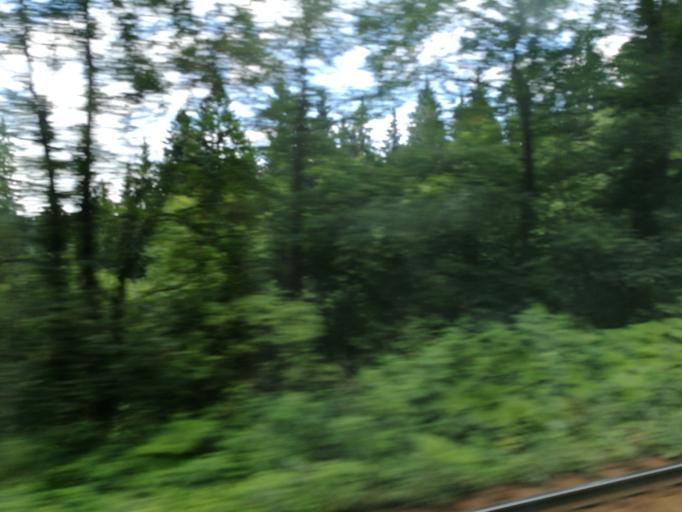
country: RO
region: Brasov
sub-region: Oras Predeal
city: Predeal
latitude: 45.5217
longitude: 25.5901
